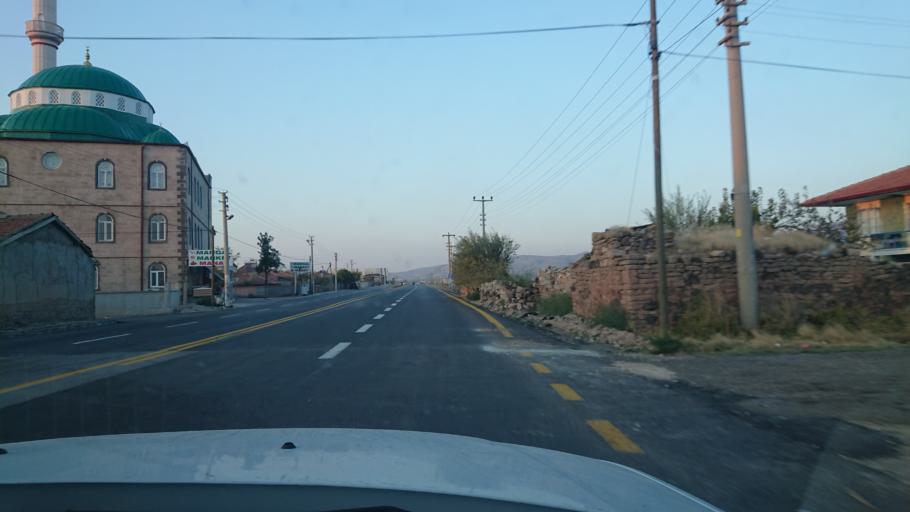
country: TR
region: Aksaray
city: Aksaray
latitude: 38.3188
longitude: 34.0531
